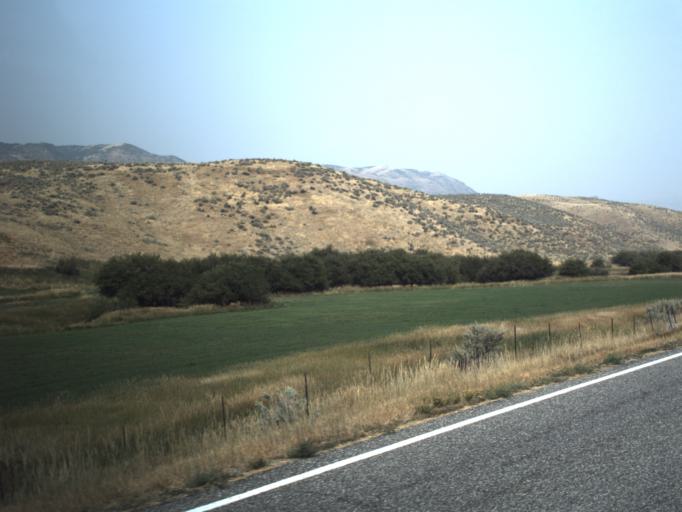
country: US
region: Utah
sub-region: Summit County
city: Coalville
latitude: 40.9978
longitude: -111.5231
